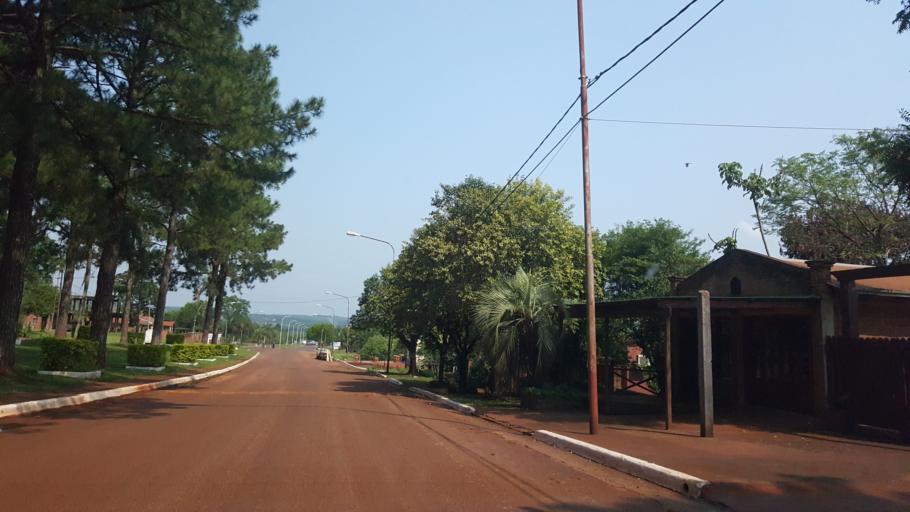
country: AR
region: Misiones
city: Santa Ana
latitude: -27.3743
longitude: -55.5781
